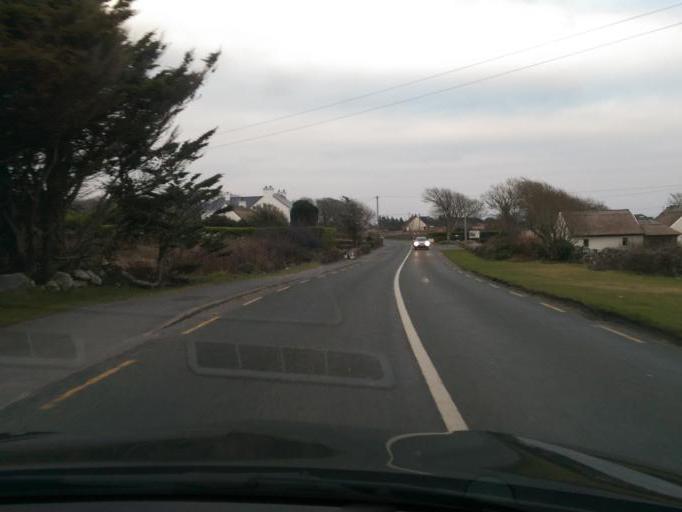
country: IE
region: Connaught
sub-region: County Galway
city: Bearna
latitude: 53.2467
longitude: -9.2743
